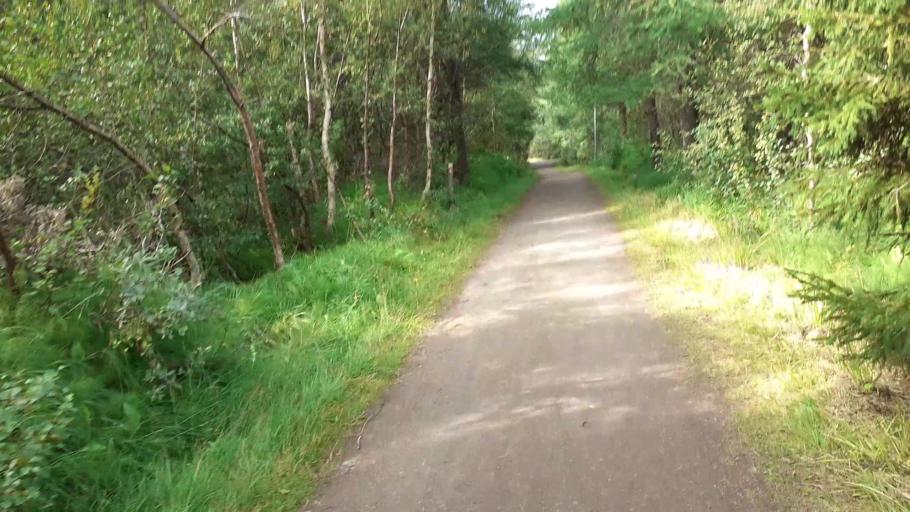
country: IS
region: Northeast
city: Akureyri
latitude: 65.6409
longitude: -18.0953
